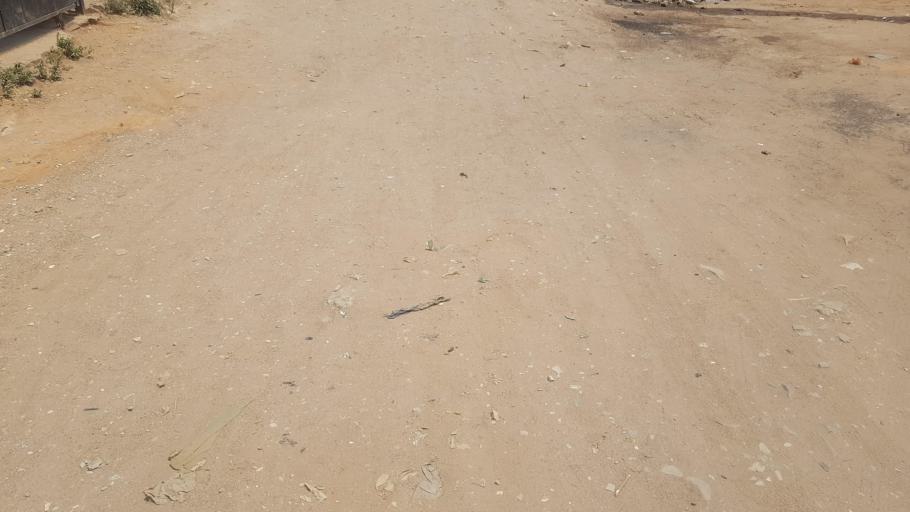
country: ZM
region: Lusaka
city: Lusaka
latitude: -15.4390
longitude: 28.3805
